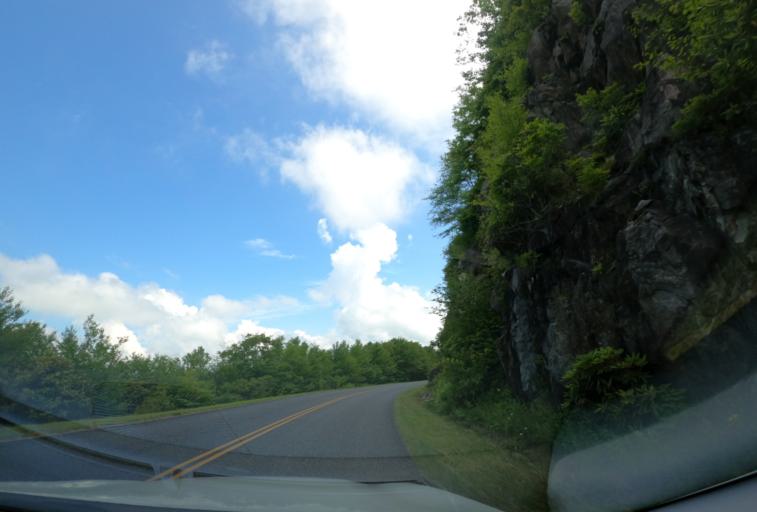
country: US
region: North Carolina
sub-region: Haywood County
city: Hazelwood
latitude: 35.3816
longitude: -83.0305
